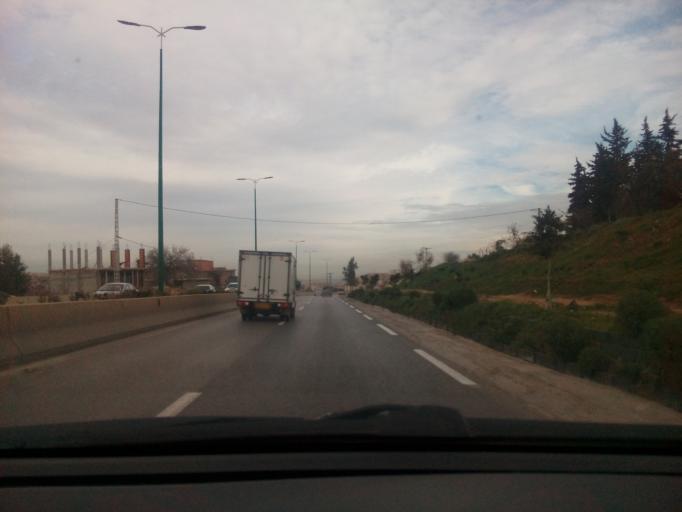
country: DZ
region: Tlemcen
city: Chetouane
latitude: 34.9128
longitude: -1.3294
